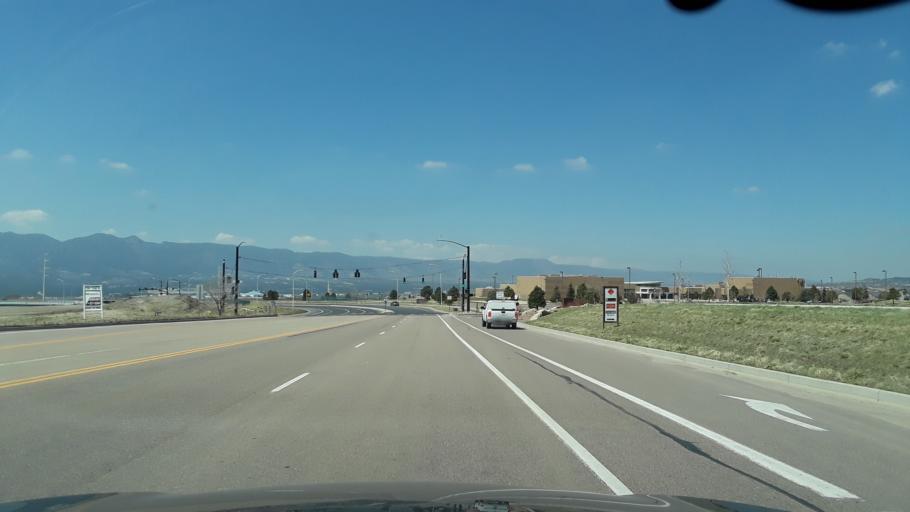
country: US
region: Colorado
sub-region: El Paso County
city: Black Forest
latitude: 38.9845
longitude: -104.7595
